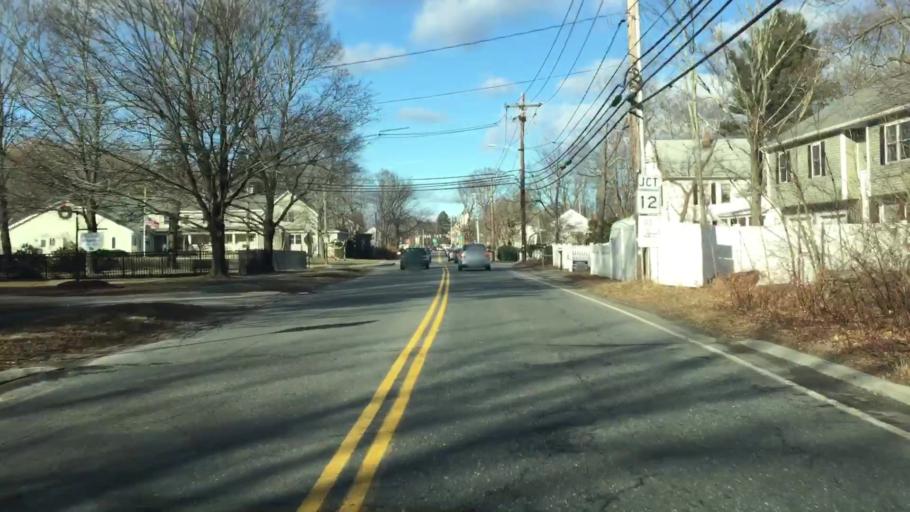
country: US
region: Massachusetts
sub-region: Worcester County
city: West Boylston
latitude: 42.3594
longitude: -71.7802
